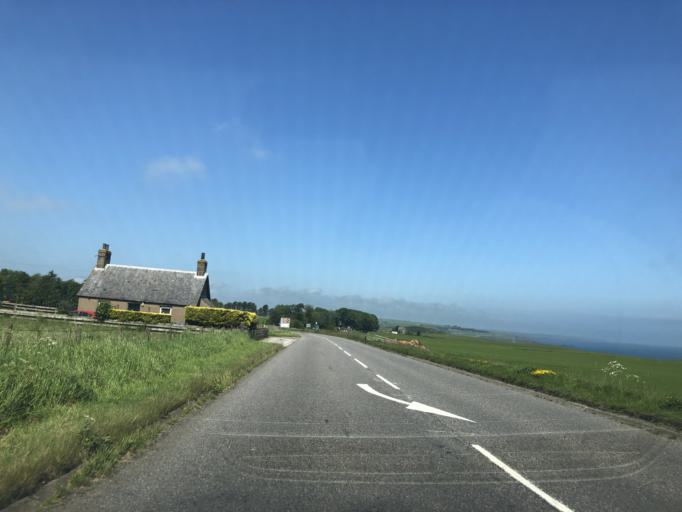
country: GB
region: Scotland
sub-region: Aberdeenshire
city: Stonehaven
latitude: 56.9392
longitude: -2.2070
